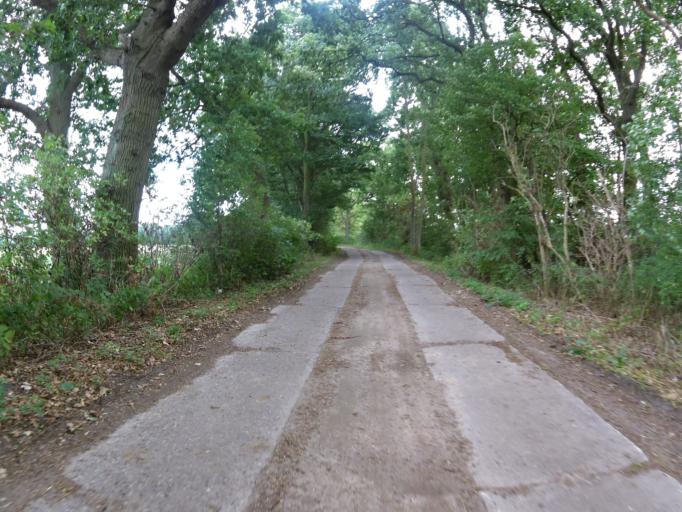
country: DE
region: Mecklenburg-Vorpommern
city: Loddin
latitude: 53.9797
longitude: 14.0652
